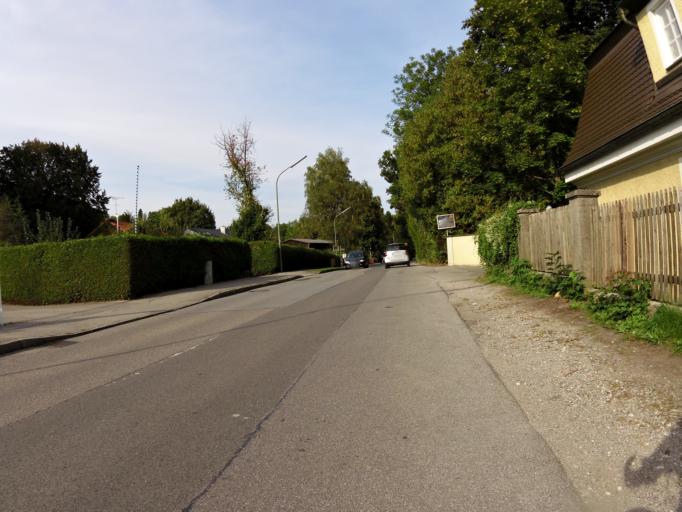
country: DE
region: Bavaria
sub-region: Upper Bavaria
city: Starnberg
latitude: 47.9853
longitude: 11.3337
